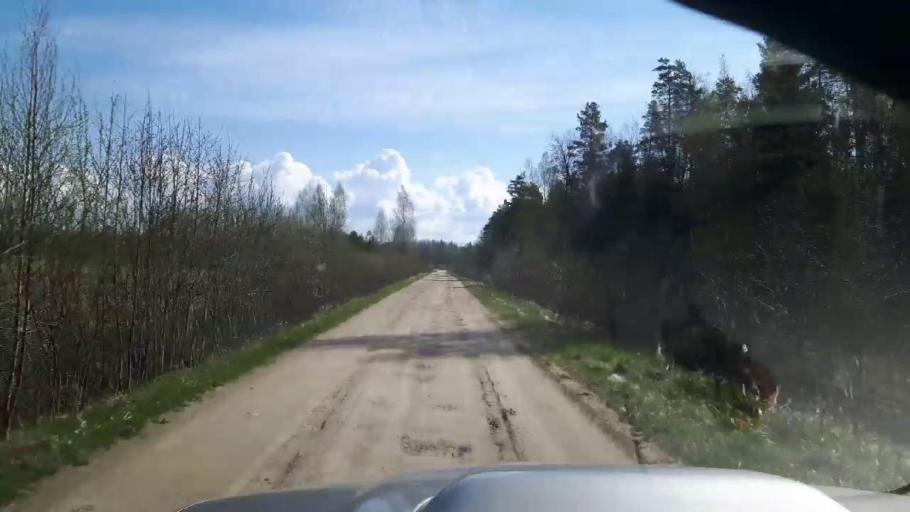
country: EE
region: Paernumaa
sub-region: Vaendra vald (alev)
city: Vandra
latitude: 58.5043
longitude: 24.9585
